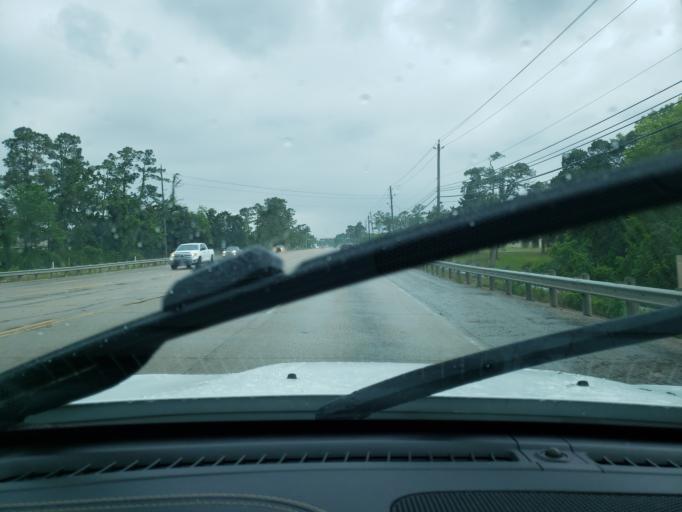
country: US
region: Texas
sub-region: Chambers County
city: Mont Belvieu
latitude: 29.7859
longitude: -94.9117
